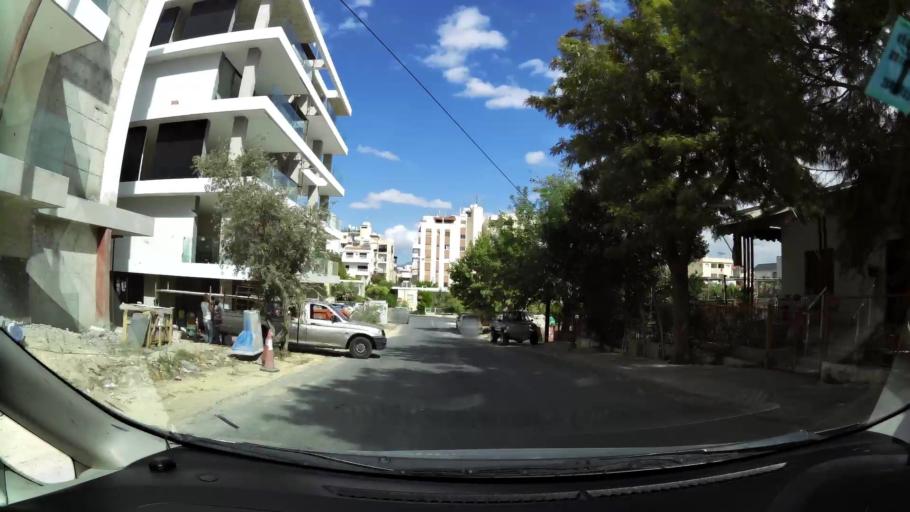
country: CY
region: Lefkosia
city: Nicosia
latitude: 35.1540
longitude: 33.3722
